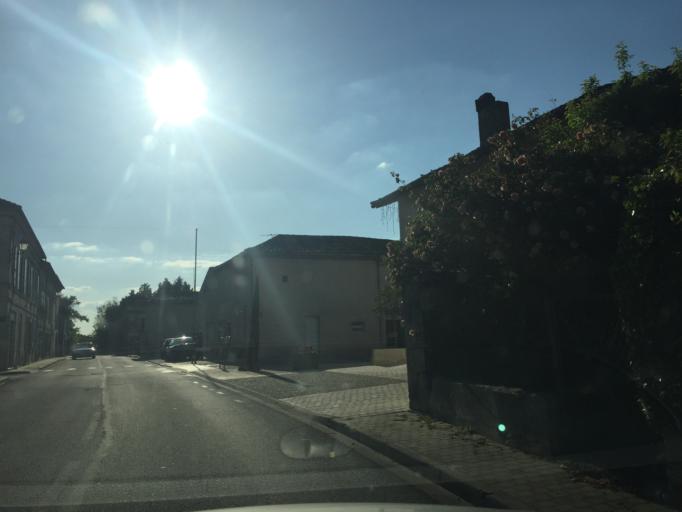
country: FR
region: Aquitaine
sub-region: Departement de la Dordogne
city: La Roche-Chalais
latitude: 45.2051
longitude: 0.0350
